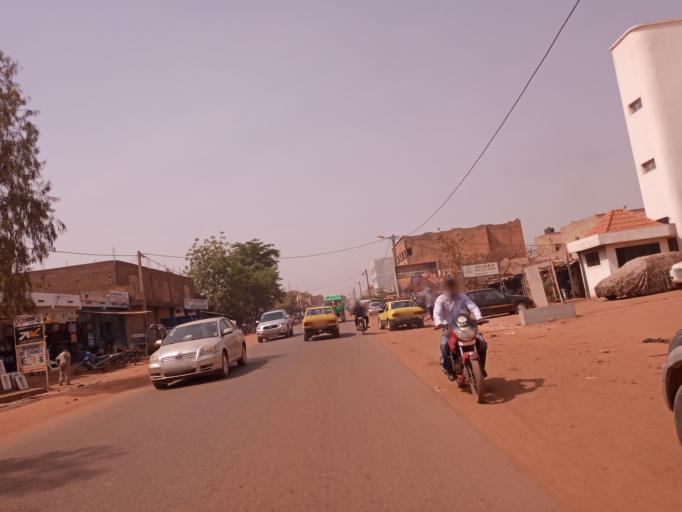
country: ML
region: Bamako
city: Bamako
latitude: 12.5927
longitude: -7.9634
